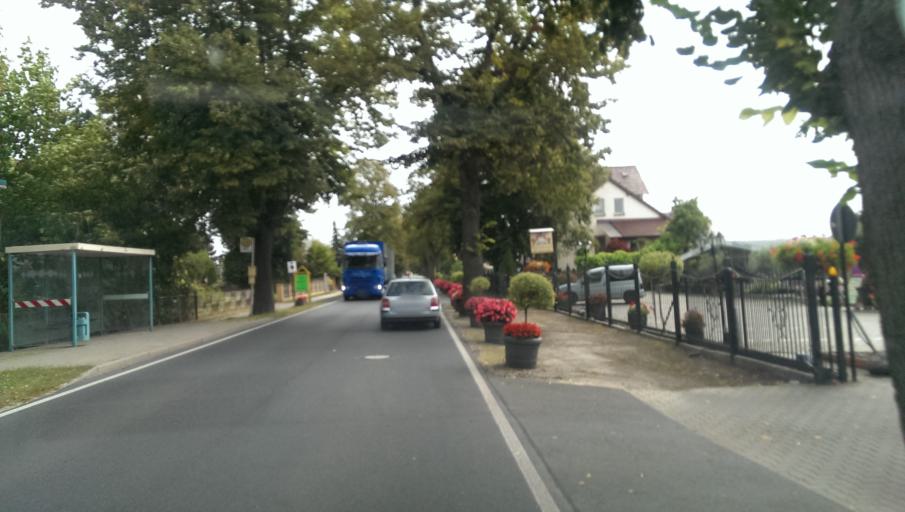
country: DE
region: Brandenburg
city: Zossen
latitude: 52.2234
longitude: 13.4223
